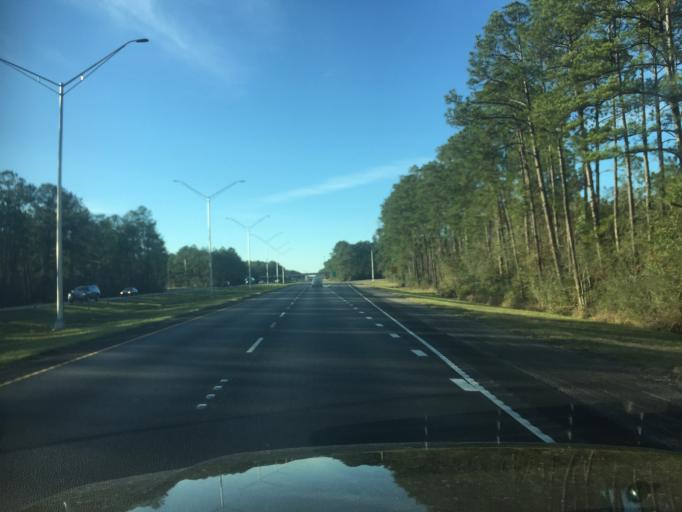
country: US
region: Louisiana
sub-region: Saint Tammany Parish
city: Lacombe
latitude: 30.3497
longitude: -89.9152
